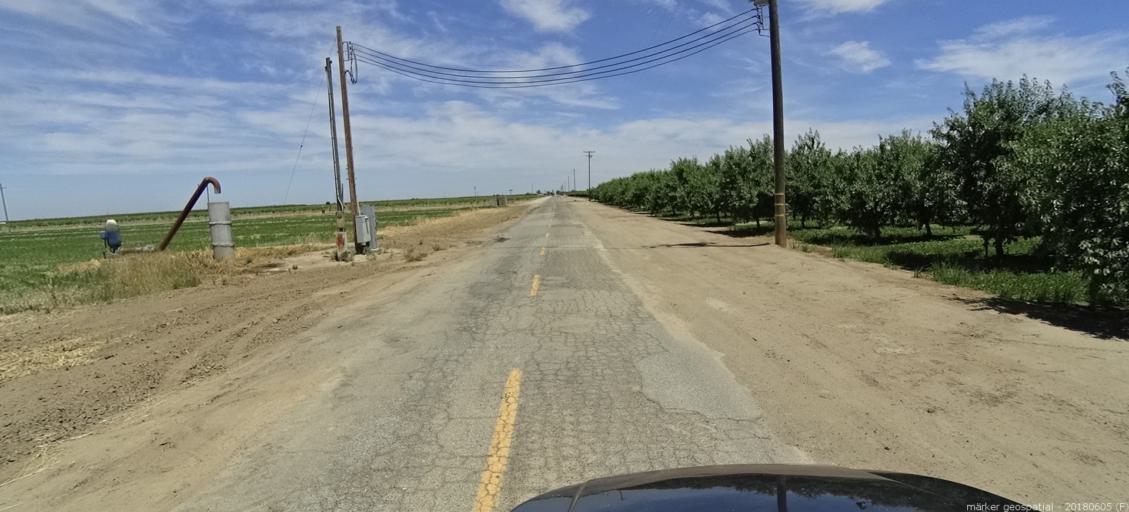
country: US
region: California
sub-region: Madera County
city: Chowchilla
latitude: 37.0894
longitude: -120.3650
